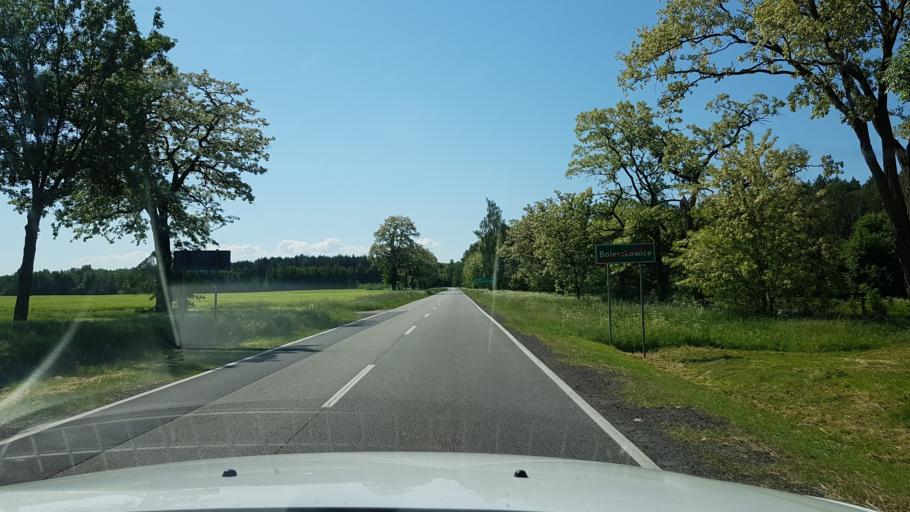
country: PL
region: West Pomeranian Voivodeship
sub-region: Powiat mysliborski
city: Boleszkowice
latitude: 52.7152
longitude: 14.5693
